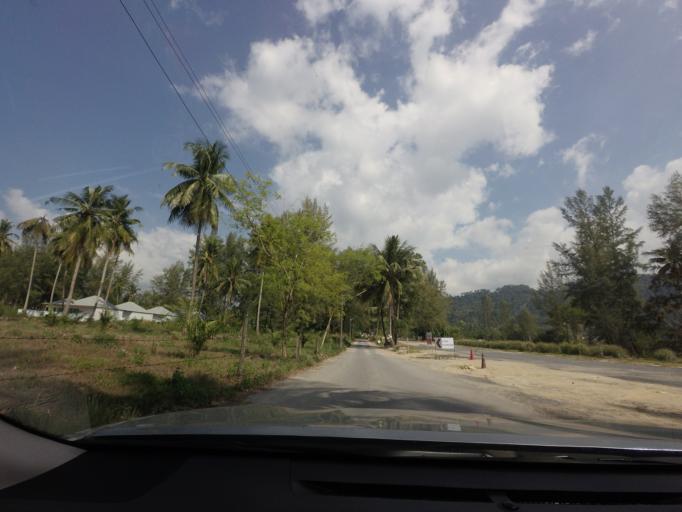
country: TH
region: Phangnga
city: Ban Khao Lak
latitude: 8.6613
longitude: 98.2486
